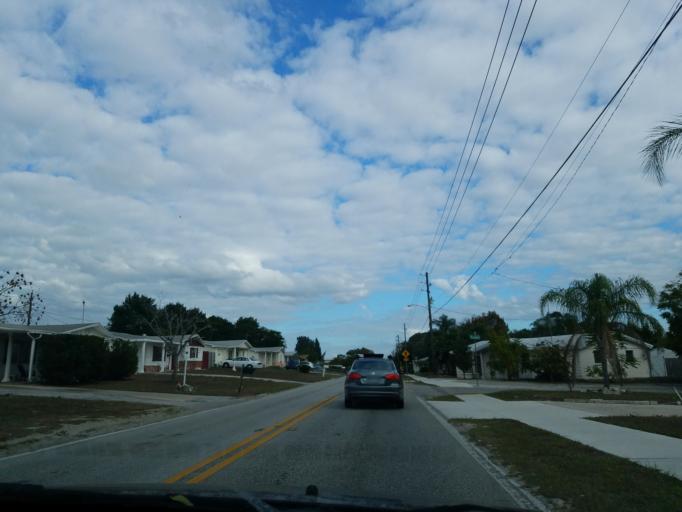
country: US
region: Florida
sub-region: Pasco County
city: Beacon Square
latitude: 28.2096
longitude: -82.7448
